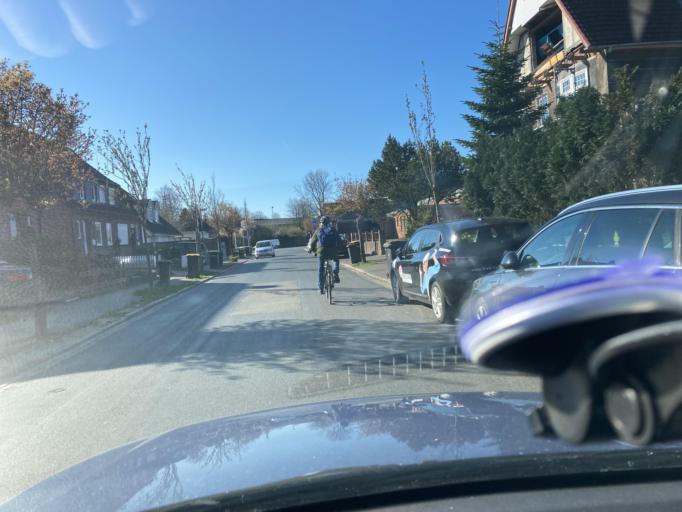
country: DE
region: Schleswig-Holstein
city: Wesseln
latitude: 54.1960
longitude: 9.0828
